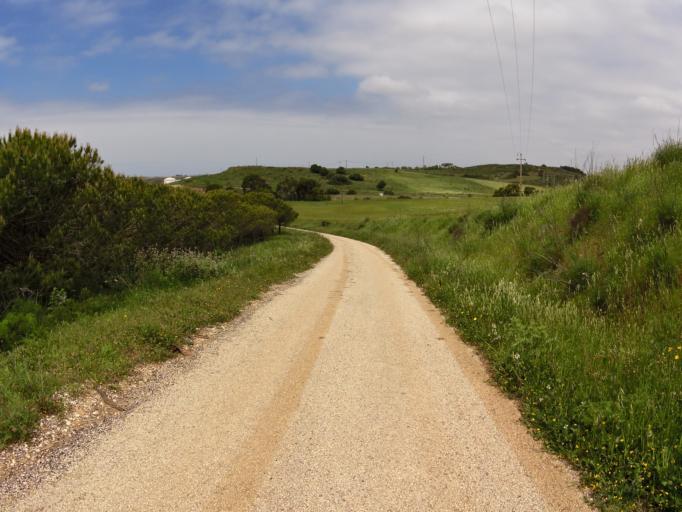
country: PT
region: Faro
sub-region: Vila do Bispo
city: Vila do Bispo
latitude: 37.0803
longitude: -8.8819
